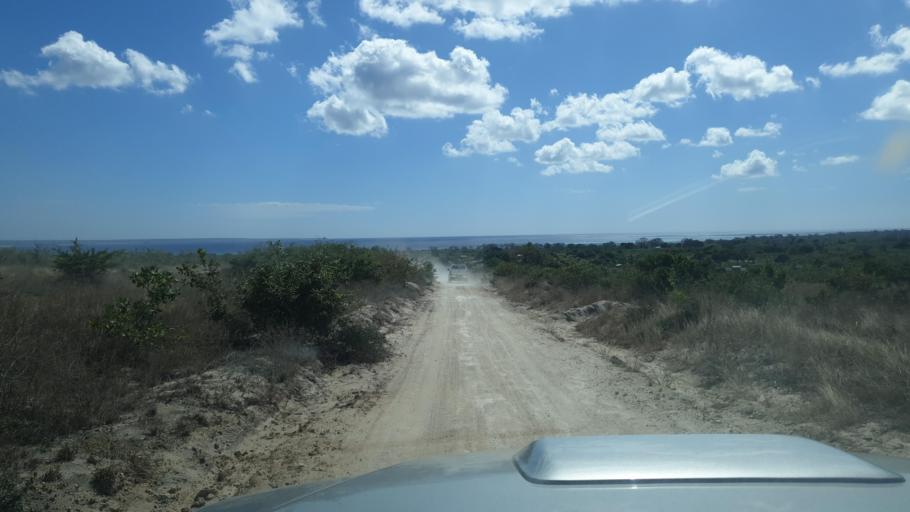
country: MZ
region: Nampula
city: Nacala
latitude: -14.4537
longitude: 40.7245
